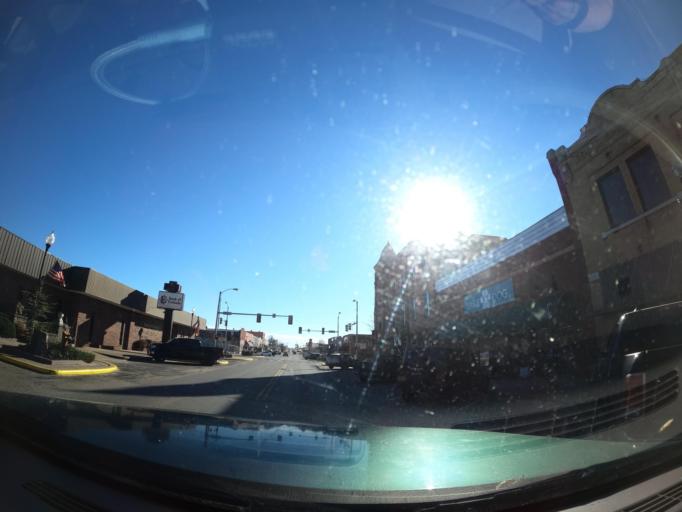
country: US
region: Oklahoma
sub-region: McIntosh County
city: Eufaula
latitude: 35.2870
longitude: -95.5825
